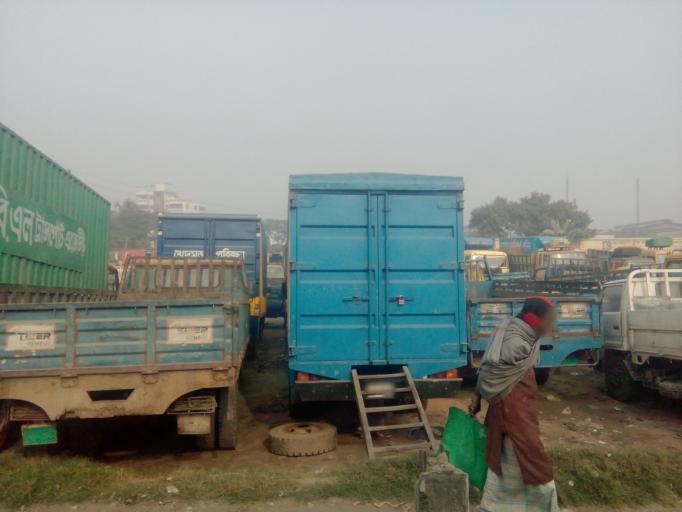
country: BD
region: Dhaka
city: Narayanganj
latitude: 23.6984
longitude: 90.5104
